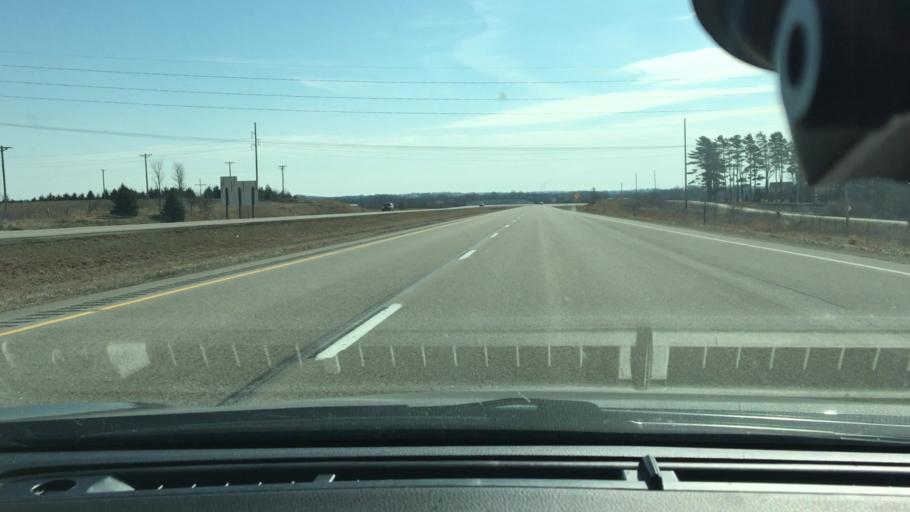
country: US
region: Iowa
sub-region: Floyd County
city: Charles City
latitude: 43.0387
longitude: -92.6663
